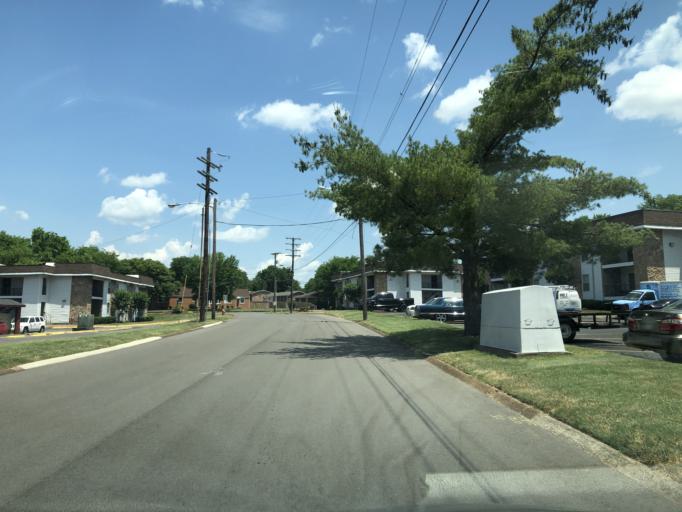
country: US
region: Tennessee
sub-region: Davidson County
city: Goodlettsville
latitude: 36.2692
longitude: -86.7017
